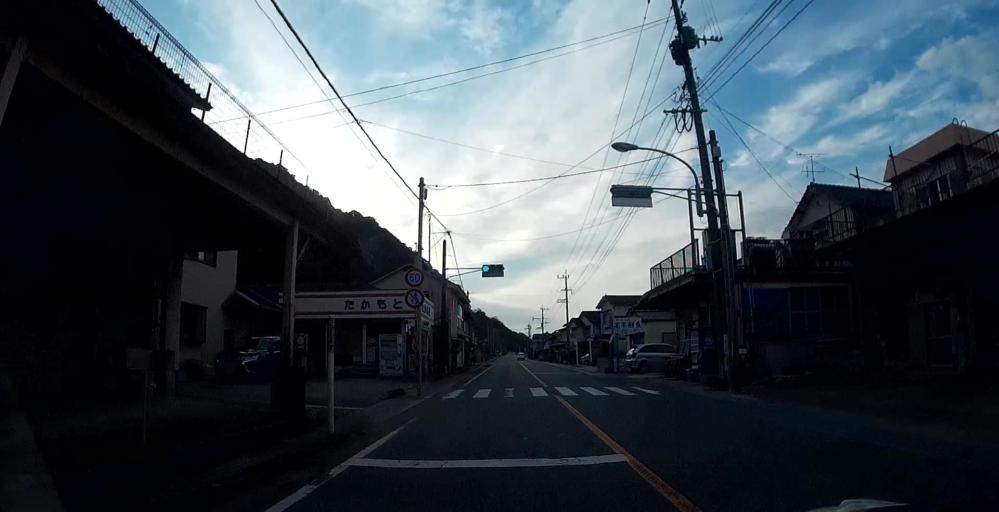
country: JP
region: Nagasaki
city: Shimabara
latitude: 32.6372
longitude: 130.4744
